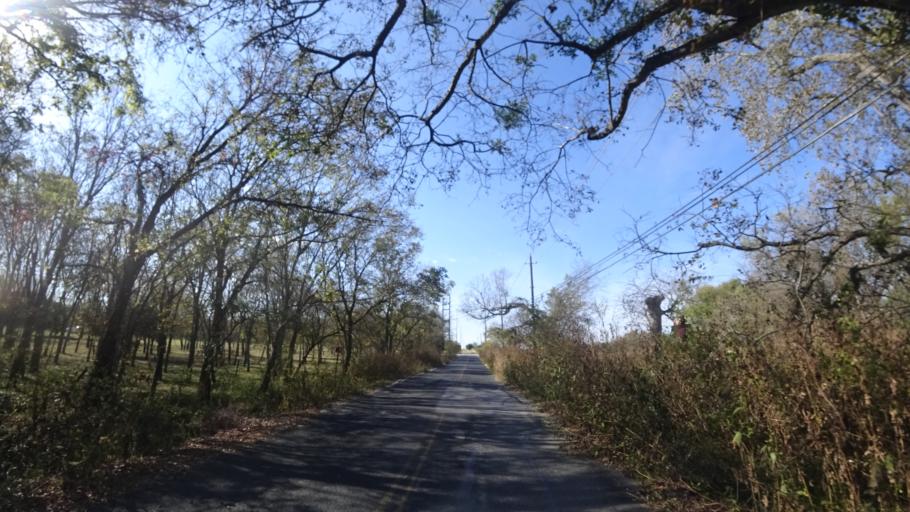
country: US
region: Texas
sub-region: Travis County
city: Pflugerville
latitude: 30.4059
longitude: -97.6404
